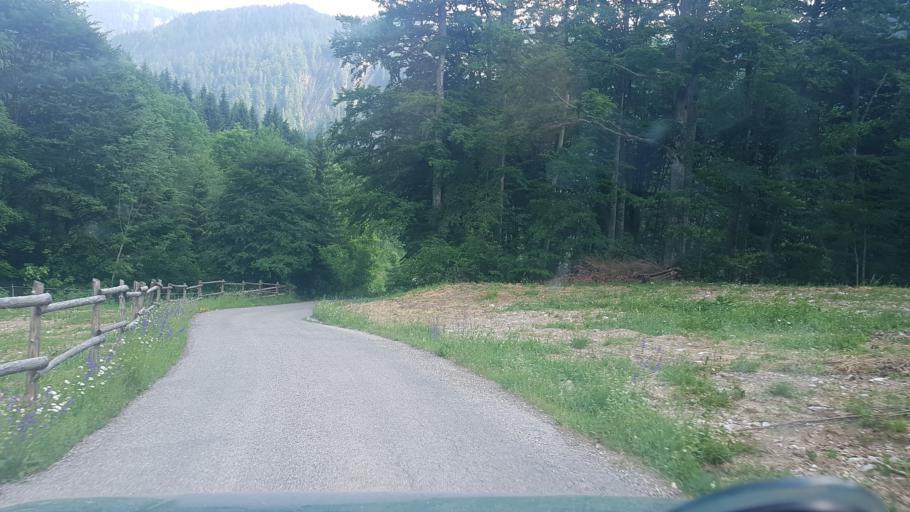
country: IT
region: Friuli Venezia Giulia
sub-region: Provincia di Udine
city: Paularo
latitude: 46.5320
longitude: 13.2103
